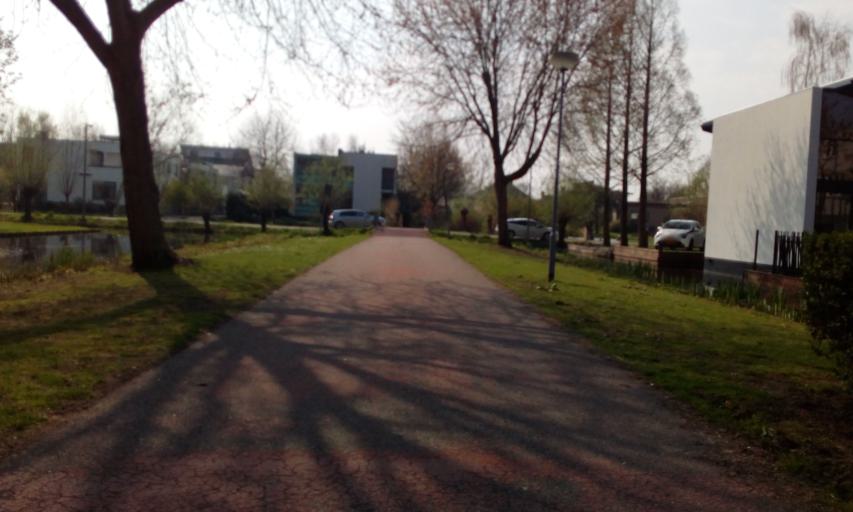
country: NL
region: South Holland
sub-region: Gemeente Rotterdam
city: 's-Gravenland
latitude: 51.9245
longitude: 4.5597
